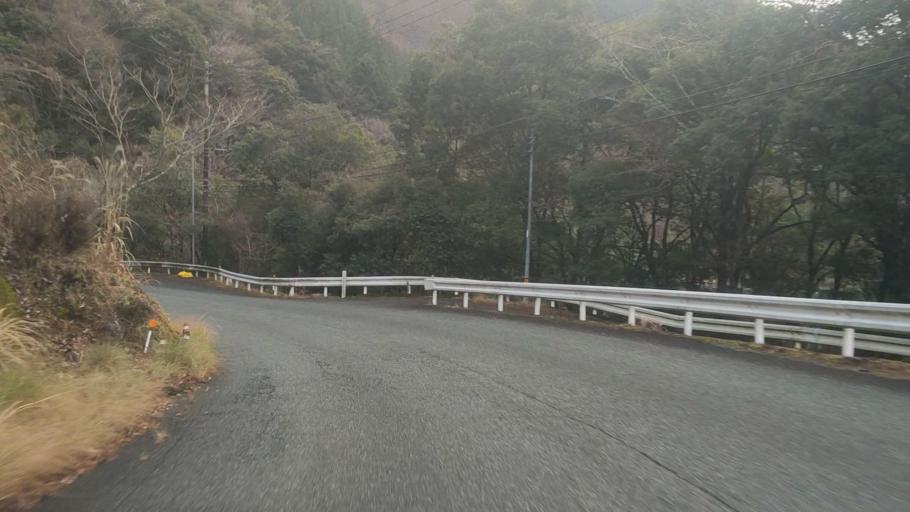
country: JP
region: Kumamoto
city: Matsubase
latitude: 32.4874
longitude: 130.8988
